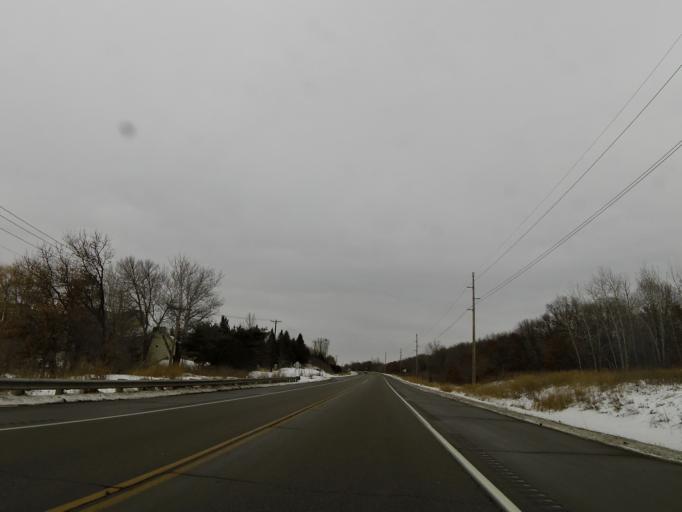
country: US
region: Minnesota
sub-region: Dakota County
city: Rosemount
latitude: 44.7837
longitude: -93.1134
